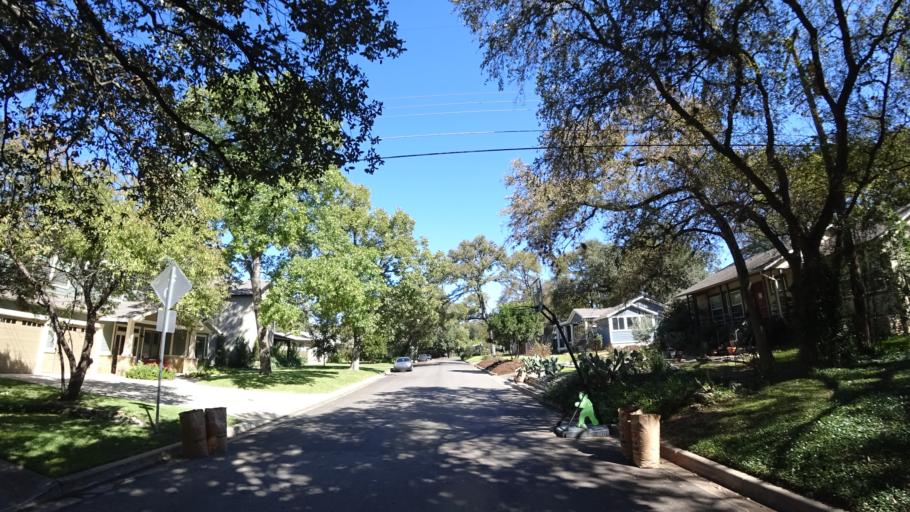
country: US
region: Texas
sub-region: Travis County
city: Austin
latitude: 30.3218
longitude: -97.7482
